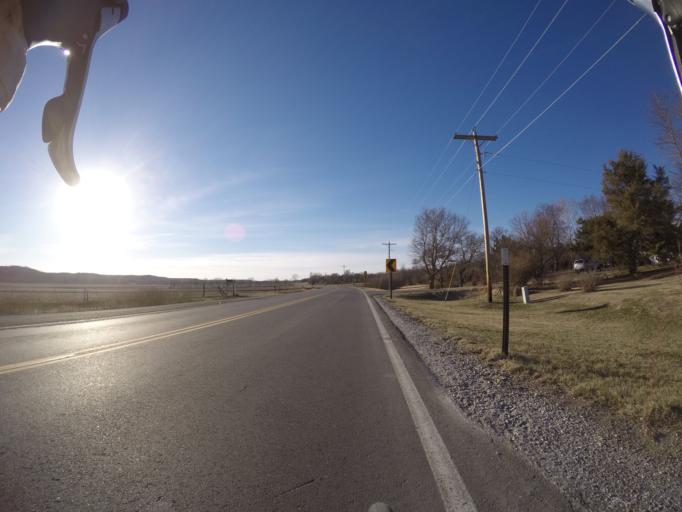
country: US
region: Kansas
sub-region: Riley County
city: Ogden
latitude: 39.2146
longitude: -96.6862
